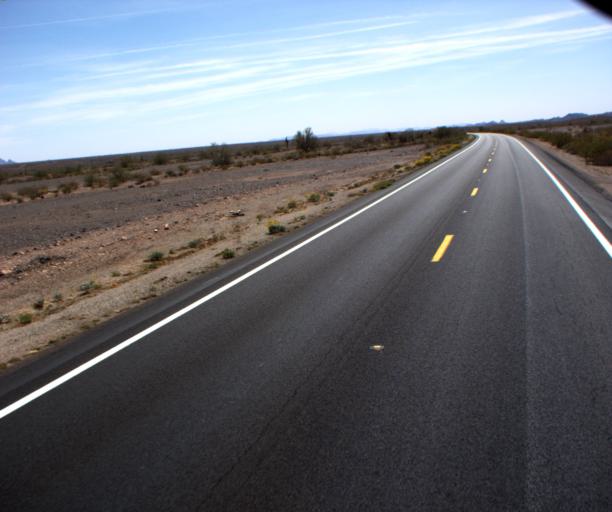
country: US
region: Arizona
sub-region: La Paz County
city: Quartzsite
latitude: 33.1890
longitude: -114.2740
